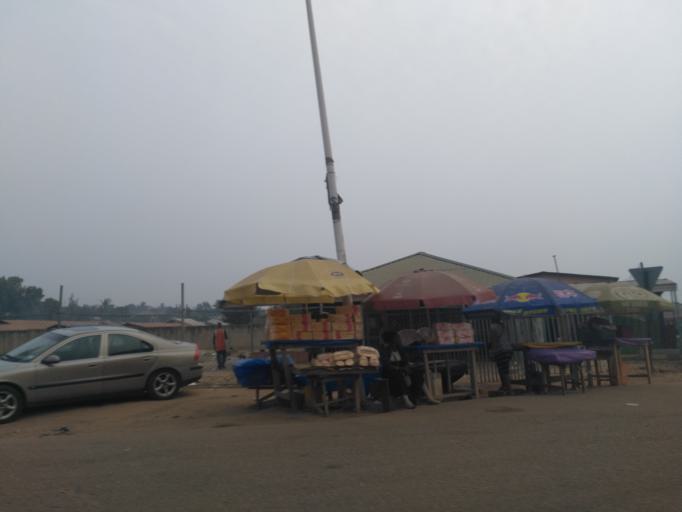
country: GH
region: Greater Accra
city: Dome
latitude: 5.6587
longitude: -0.2662
